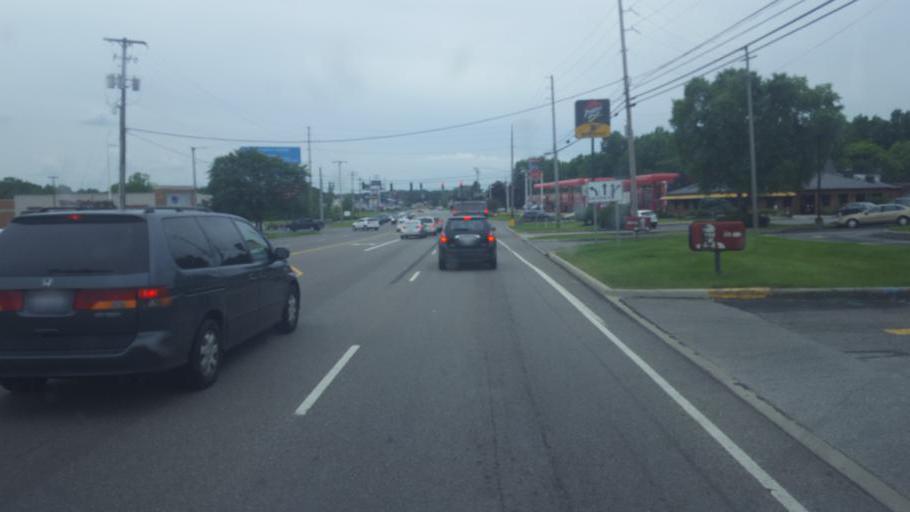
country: US
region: Ohio
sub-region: Trumbull County
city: Morgandale
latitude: 41.2664
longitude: -80.7828
